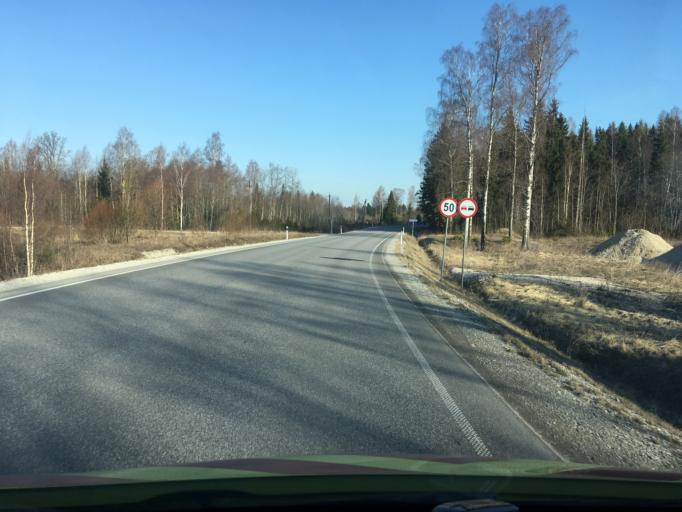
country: EE
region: Raplamaa
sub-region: Rapla vald
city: Rapla
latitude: 59.0101
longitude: 24.8381
